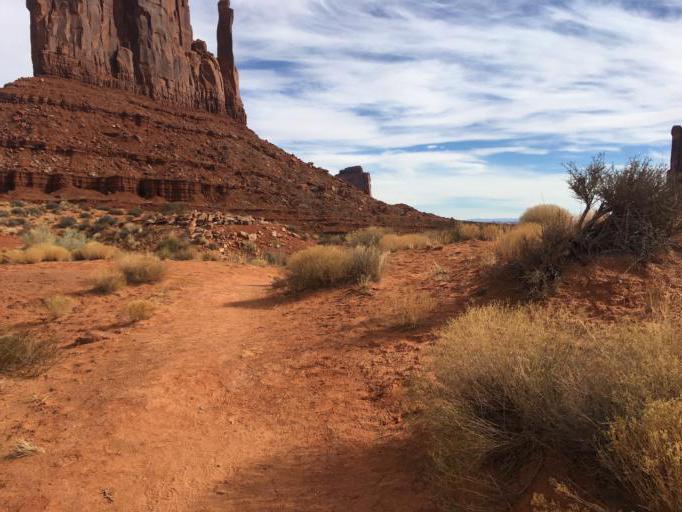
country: US
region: Arizona
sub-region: Navajo County
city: Kayenta
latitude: 36.9883
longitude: -110.1020
